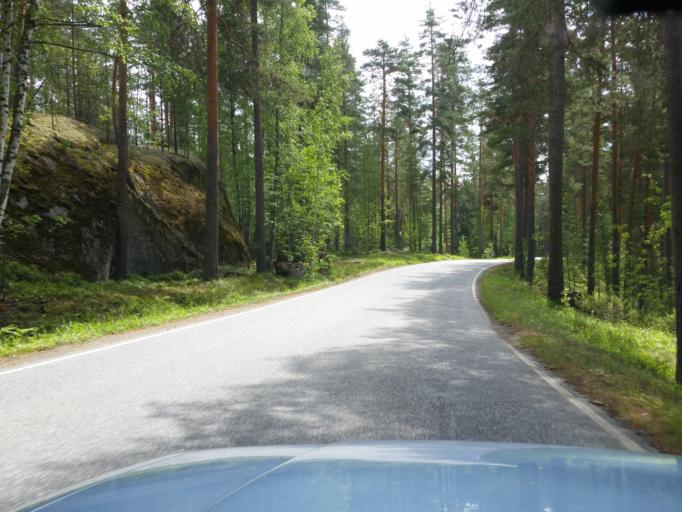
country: FI
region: Southern Savonia
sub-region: Savonlinna
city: Sulkava
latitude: 61.7922
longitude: 28.4231
